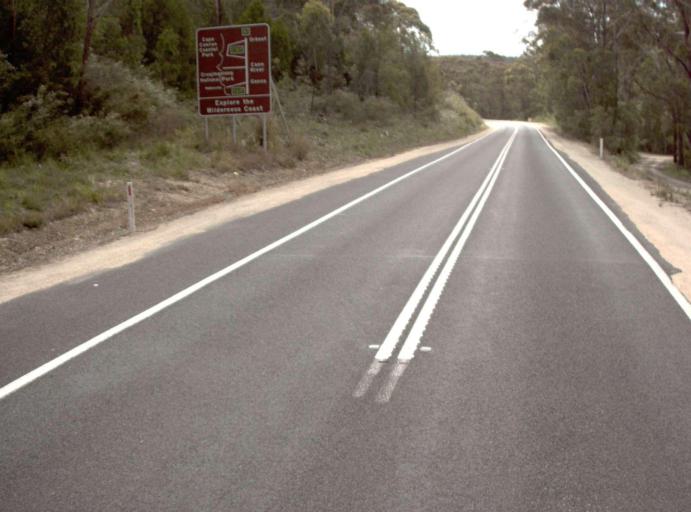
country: AU
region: New South Wales
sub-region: Bega Valley
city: Eden
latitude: -37.4591
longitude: 149.5973
